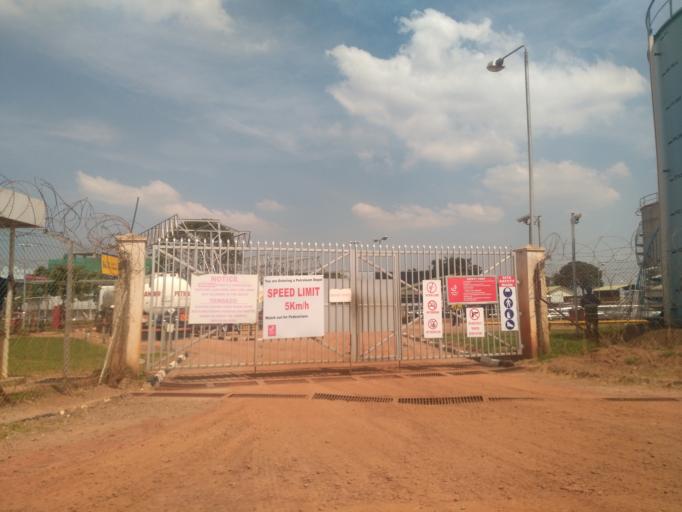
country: UG
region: Central Region
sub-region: Wakiso District
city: Entebbe
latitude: 0.0424
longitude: 32.4444
